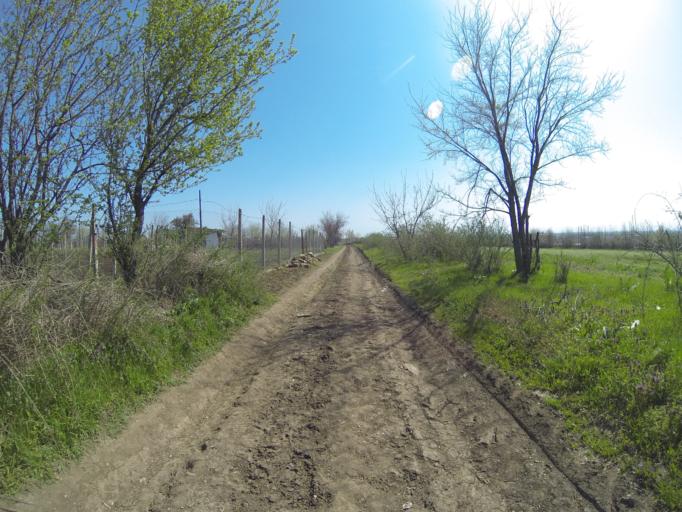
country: RO
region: Dolj
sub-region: Comuna Segarcea
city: Segarcea
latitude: 44.1040
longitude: 23.7270
